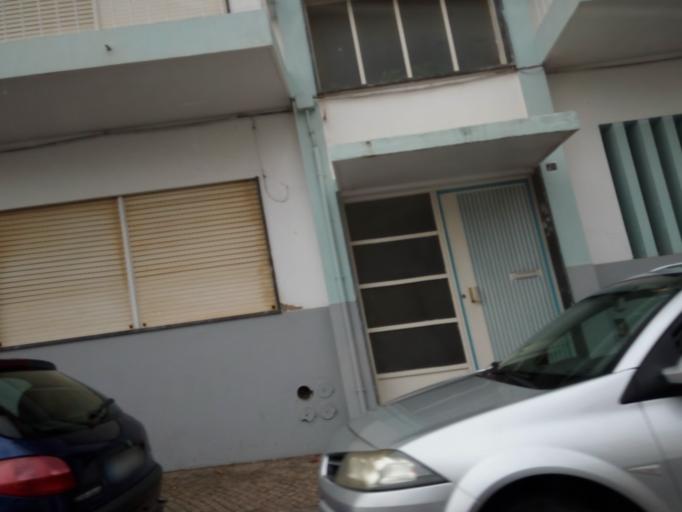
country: PT
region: Faro
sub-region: Loule
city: Loule
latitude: 37.1350
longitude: -8.0126
